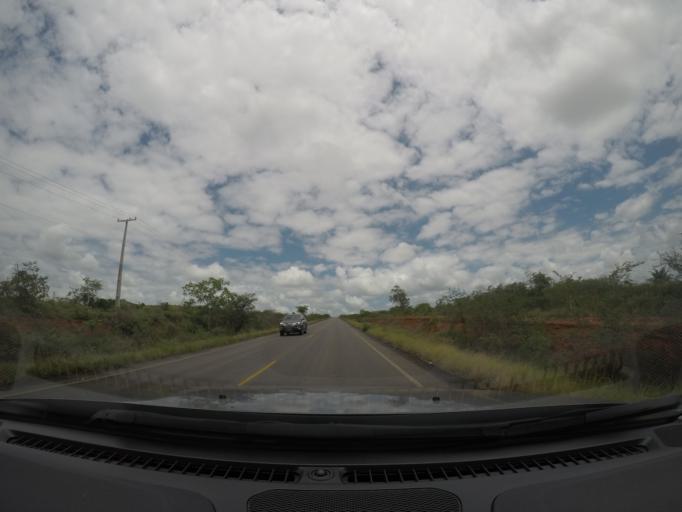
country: BR
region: Bahia
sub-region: Itaberaba
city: Itaberaba
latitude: -12.4569
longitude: -40.1559
